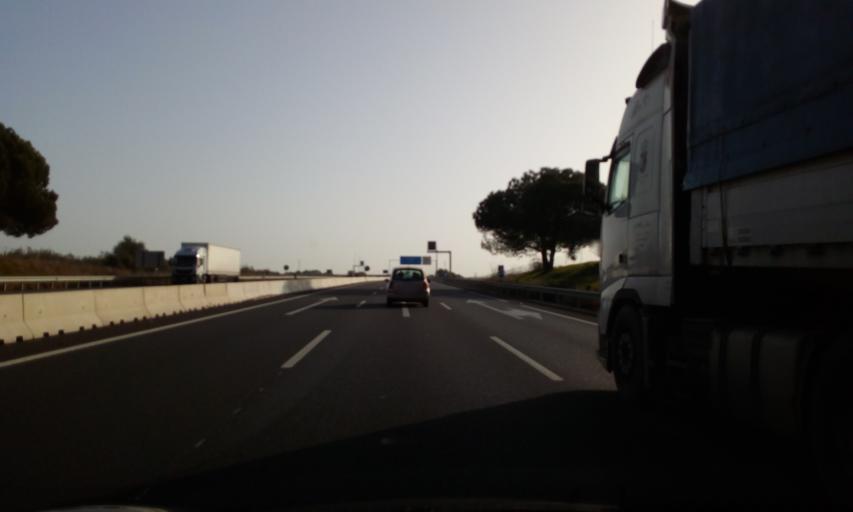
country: ES
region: Andalusia
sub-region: Provincia de Sevilla
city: Benacazon
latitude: 37.3577
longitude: -6.1807
